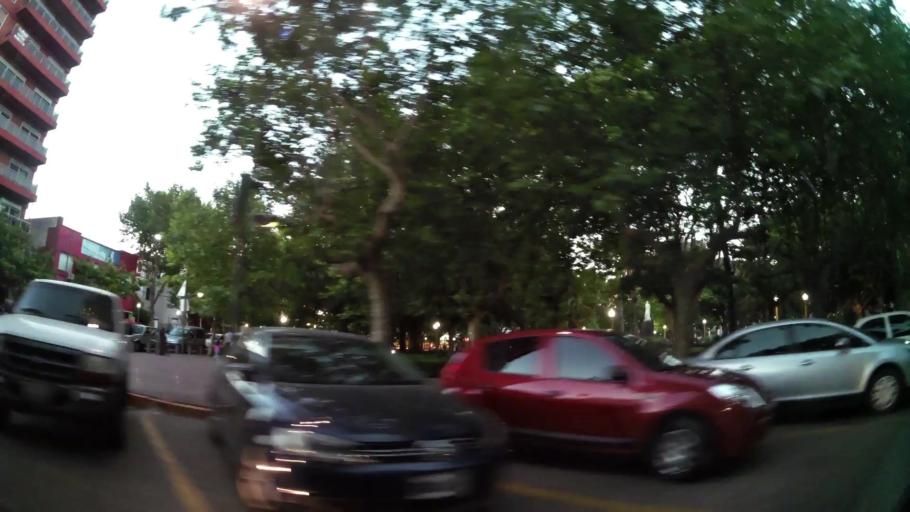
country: AR
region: Buenos Aires
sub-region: Partido de Tigre
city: Tigre
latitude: -34.4408
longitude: -58.5586
